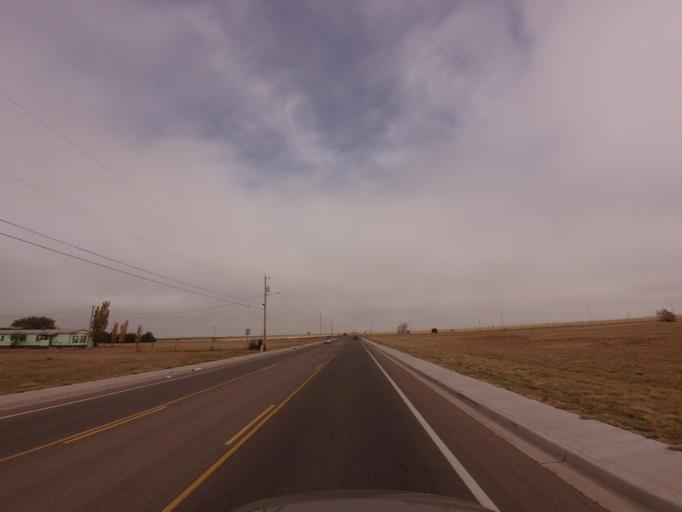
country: US
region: New Mexico
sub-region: Curry County
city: Clovis
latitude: 34.4324
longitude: -103.2317
